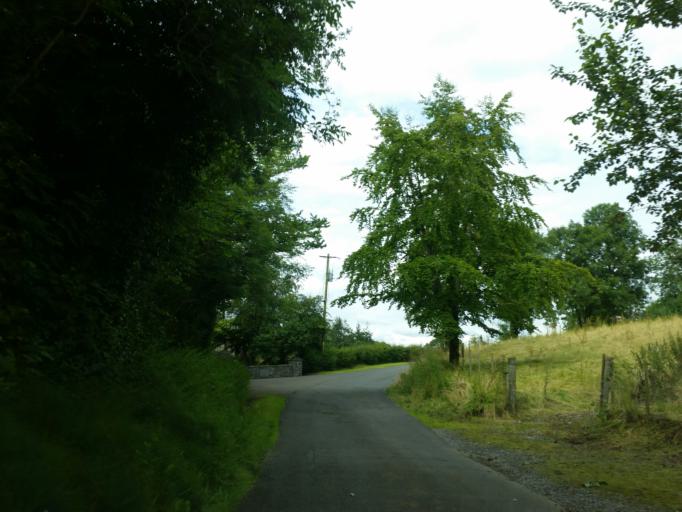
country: IE
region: Ulster
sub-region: County Monaghan
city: Clones
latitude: 54.2006
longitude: -7.2492
